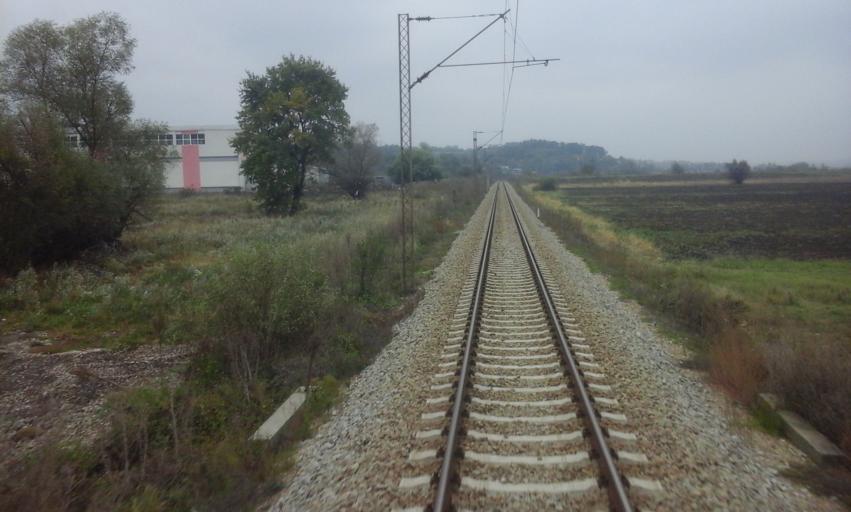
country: RS
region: Central Serbia
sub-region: Belgrade
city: Mladenovac
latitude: 44.4936
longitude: 20.6513
